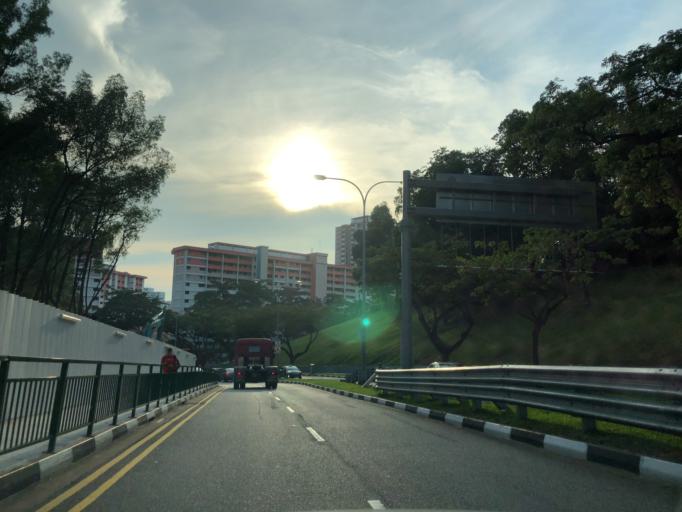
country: SG
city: Singapore
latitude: 1.2787
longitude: 103.8327
